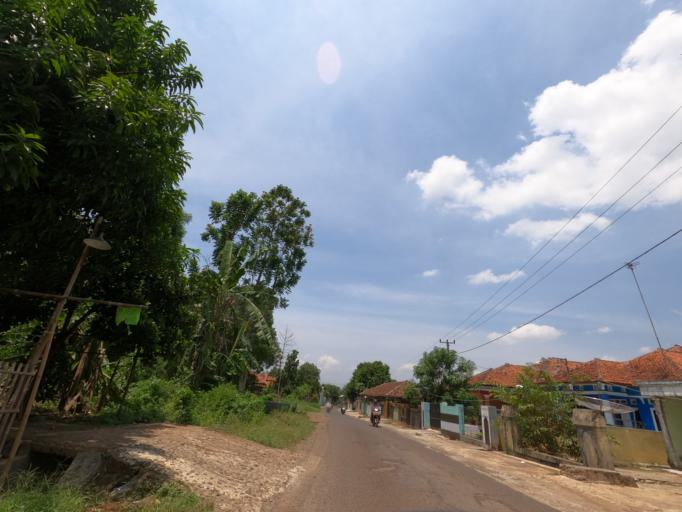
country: ID
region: West Java
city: Pamanukan
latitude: -6.5175
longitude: 107.7755
